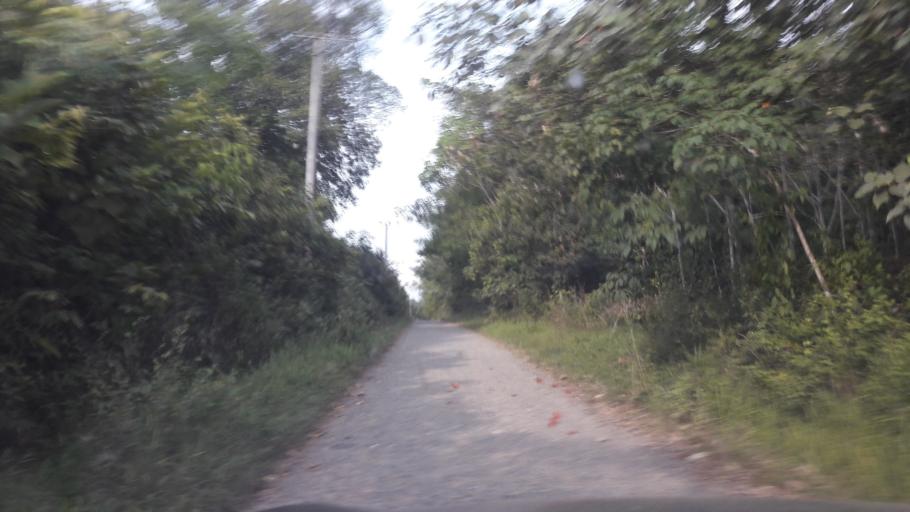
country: ID
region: South Sumatra
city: Gunungmenang
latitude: -3.2451
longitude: 104.0040
